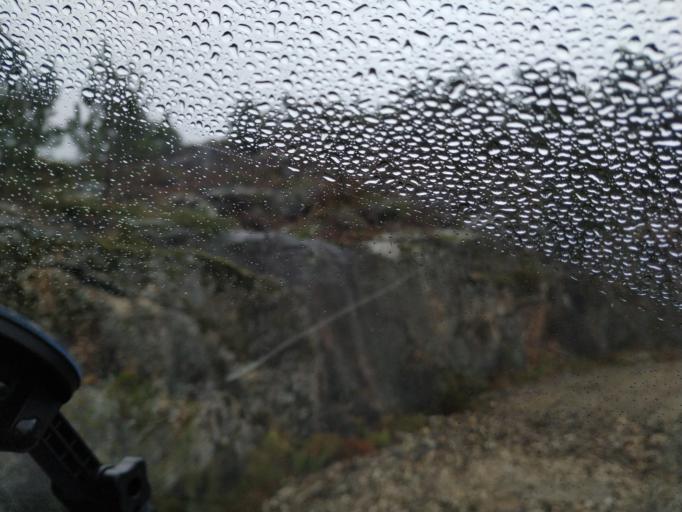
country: PT
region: Vila Real
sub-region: Vila Real
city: Vila Real
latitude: 41.3729
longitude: -7.7463
